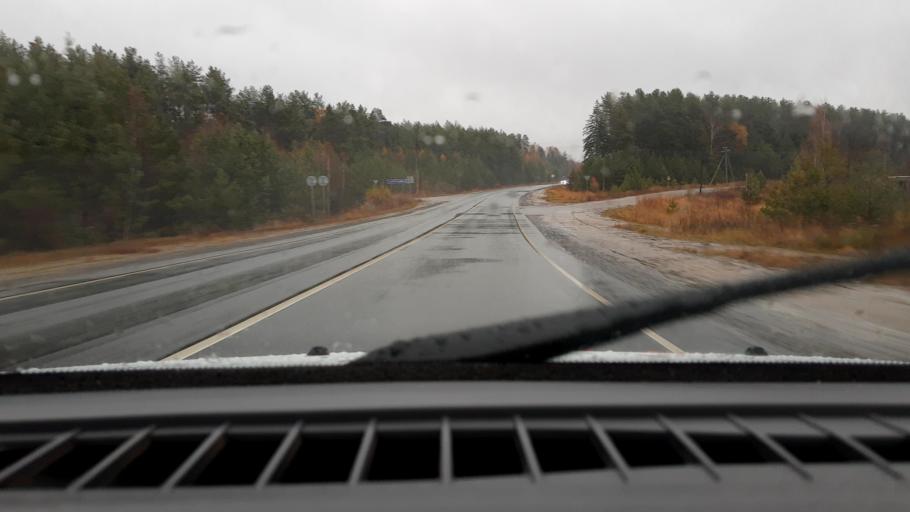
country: RU
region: Nizjnij Novgorod
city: Linda
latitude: 56.6908
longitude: 44.1883
